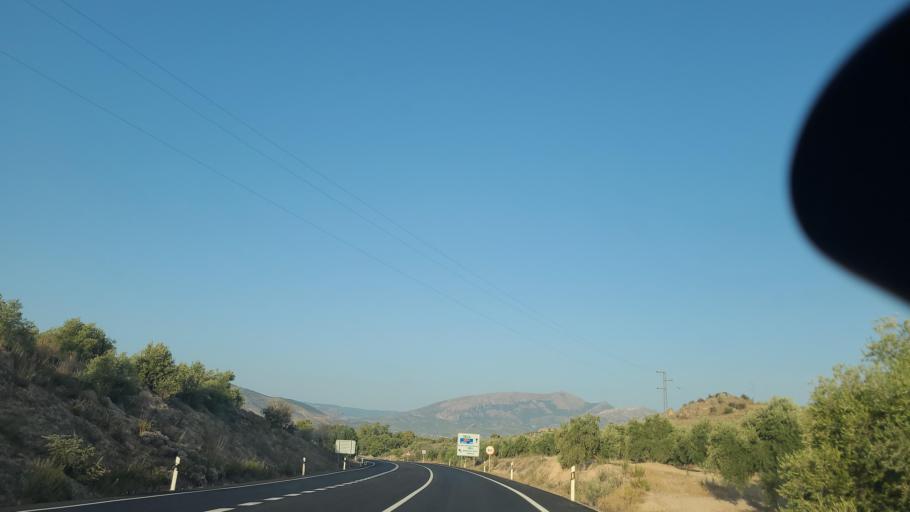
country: ES
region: Andalusia
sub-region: Provincia de Jaen
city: Mancha Real
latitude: 37.8039
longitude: -3.6571
